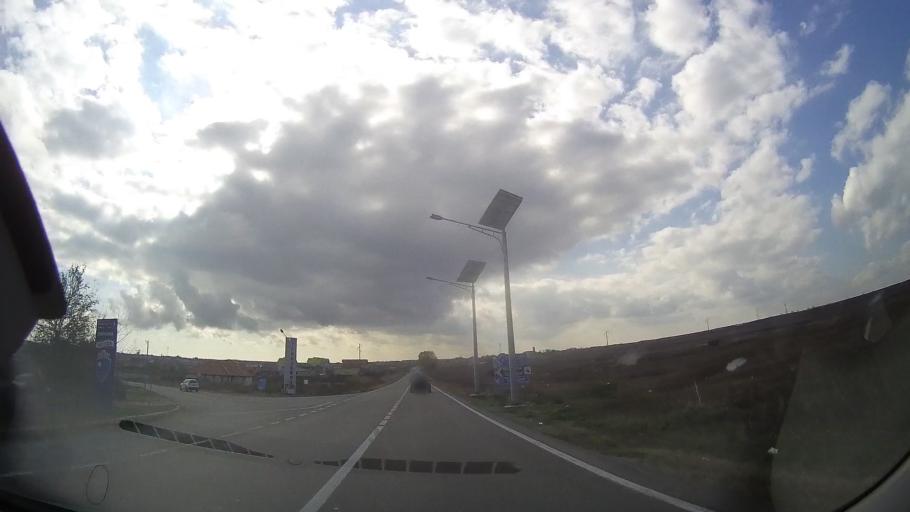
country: RO
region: Constanta
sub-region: Oras Techirghiol
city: Techirghiol
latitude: 44.0659
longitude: 28.5936
